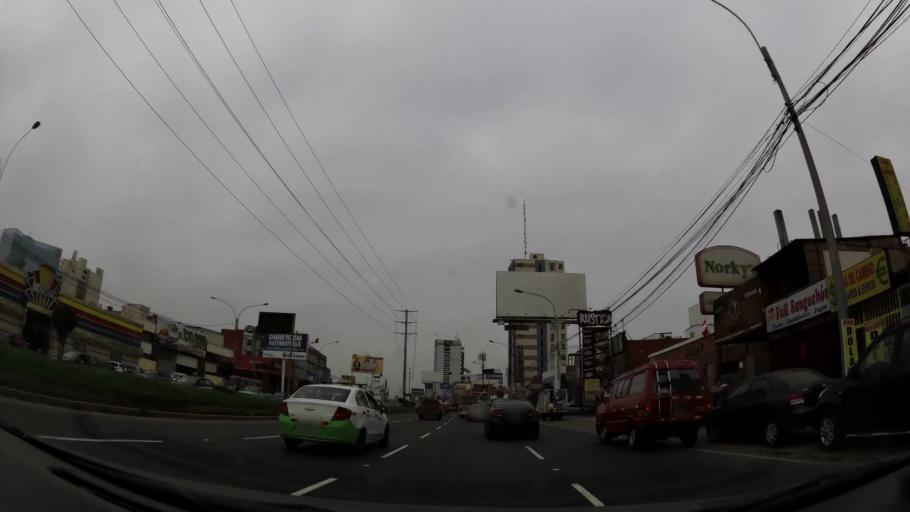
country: PE
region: Callao
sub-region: Callao
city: Callao
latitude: -12.0779
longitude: -77.0921
